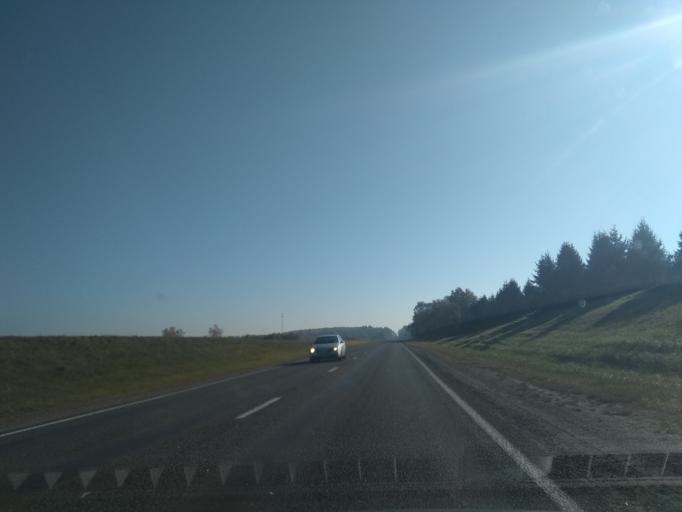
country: BY
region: Grodnenskaya
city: Slonim
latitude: 53.1146
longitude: 25.1491
